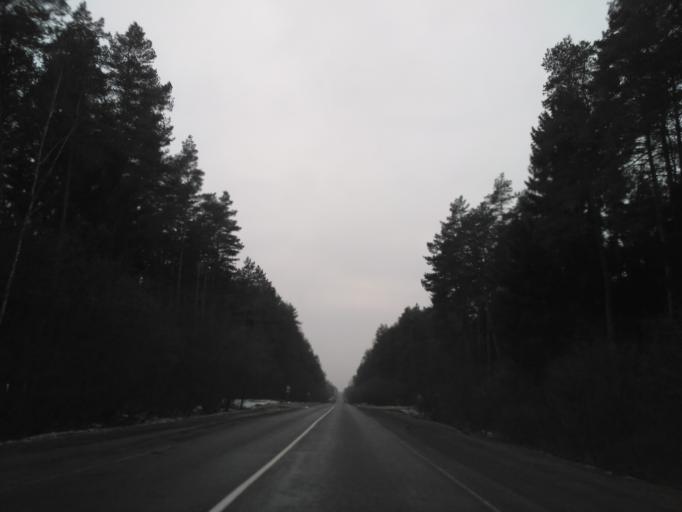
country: BY
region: Minsk
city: Snow
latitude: 53.2805
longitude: 26.3578
